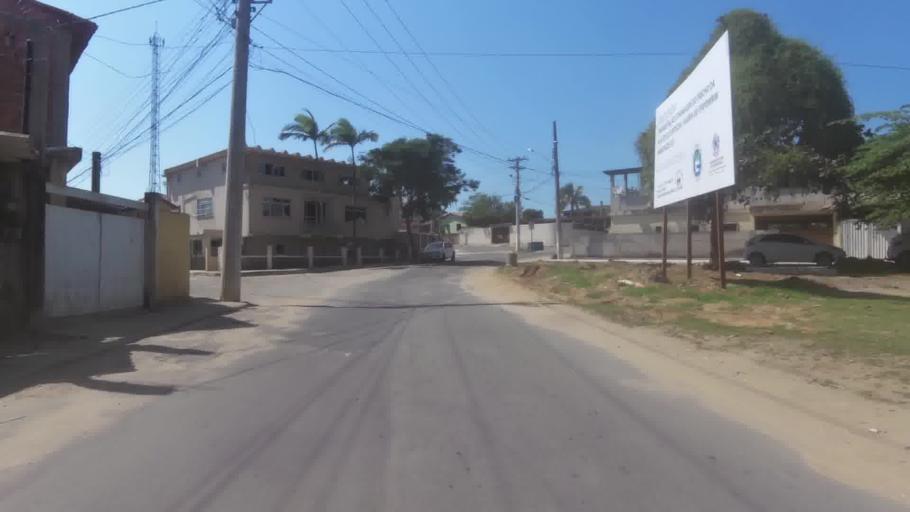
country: BR
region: Espirito Santo
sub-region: Itapemirim
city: Itapemirim
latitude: -21.0096
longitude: -40.8140
